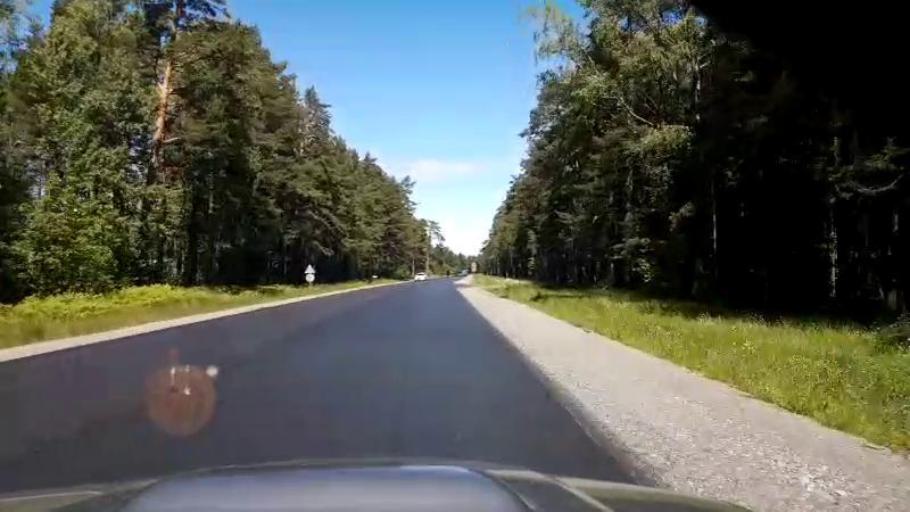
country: LV
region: Salacgrivas
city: Ainazi
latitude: 57.8282
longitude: 24.3447
